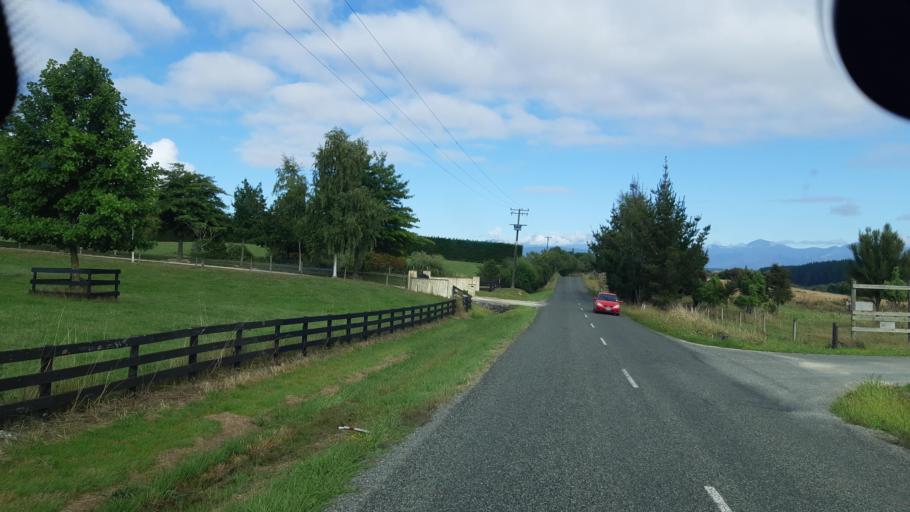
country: NZ
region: Tasman
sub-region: Tasman District
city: Mapua
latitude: -41.2441
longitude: 173.0509
